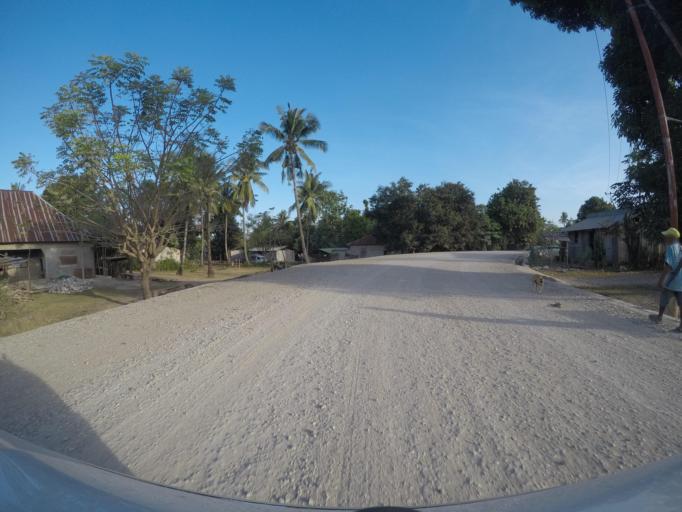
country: TL
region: Viqueque
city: Viqueque
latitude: -8.8455
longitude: 126.5127
